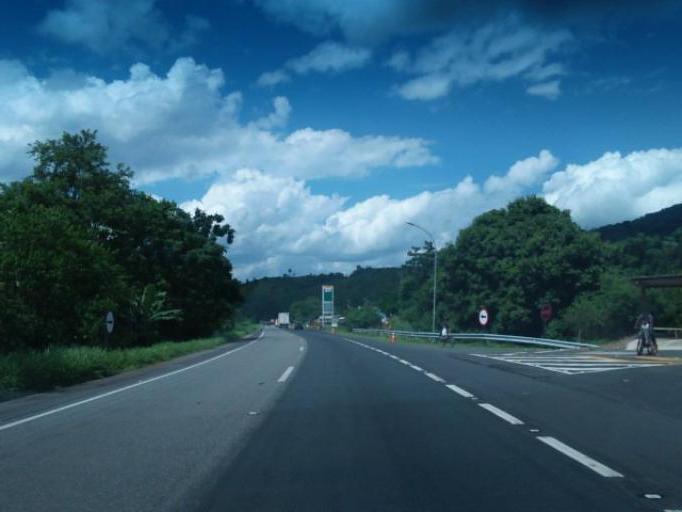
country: BR
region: Sao Paulo
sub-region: Cajati
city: Cajati
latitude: -24.7872
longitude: -48.1771
